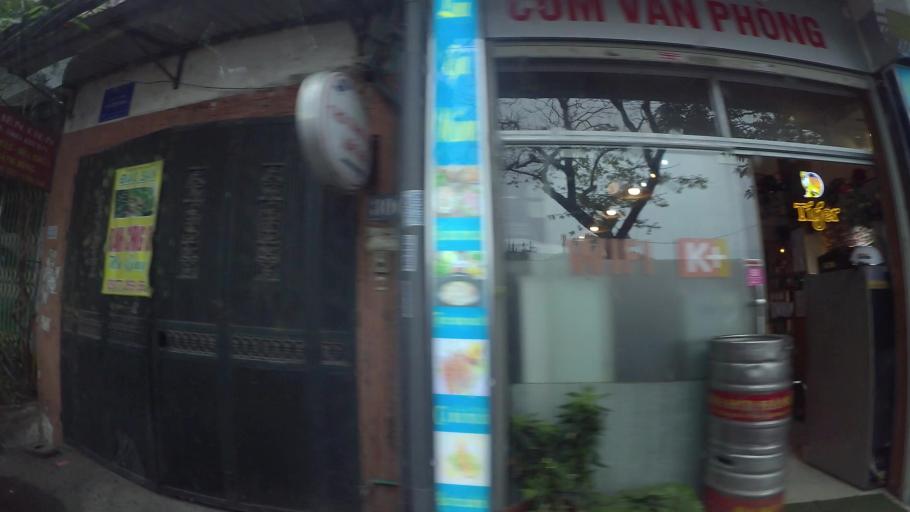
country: VN
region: Ha Noi
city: Dong Da
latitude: 21.0176
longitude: 105.8177
